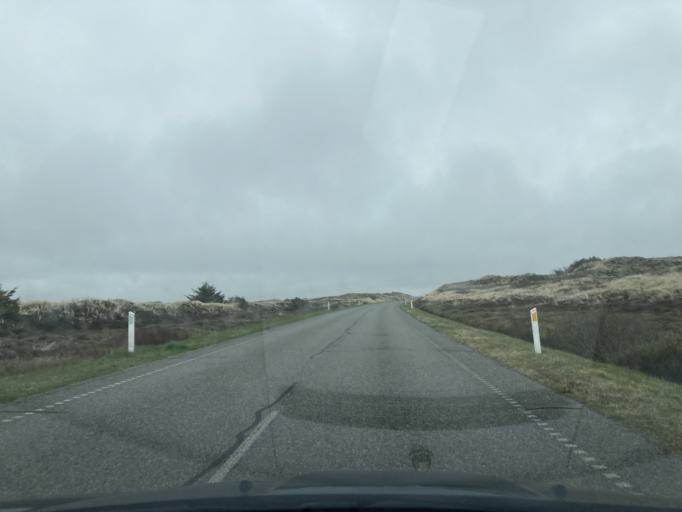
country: DK
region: North Denmark
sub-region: Thisted Kommune
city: Hurup
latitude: 56.9266
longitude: 8.3560
